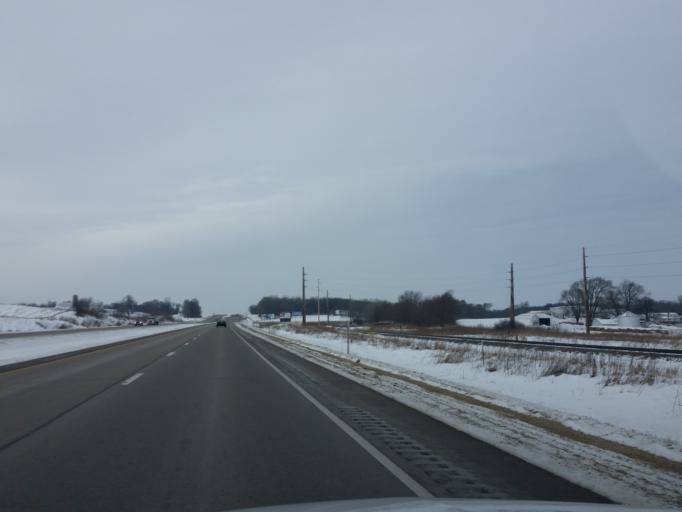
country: US
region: Iowa
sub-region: Dubuque County
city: Dyersville
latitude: 42.4636
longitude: -91.0690
